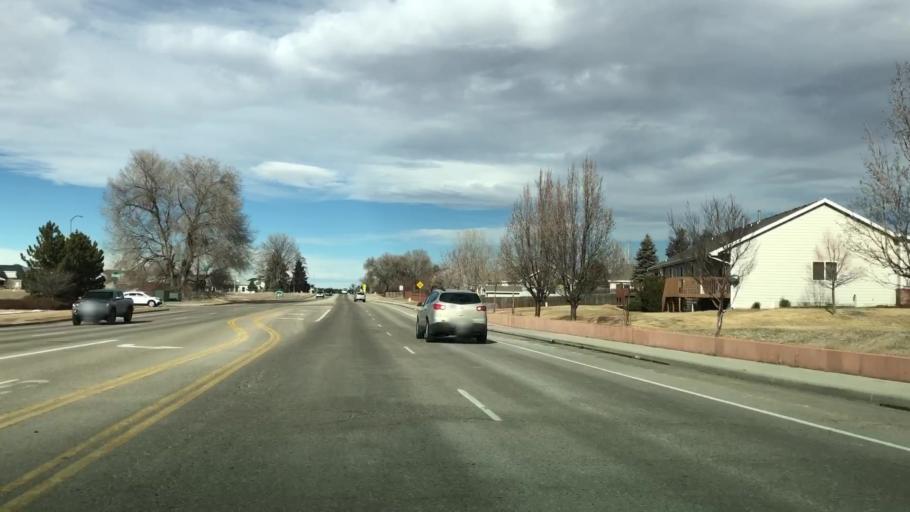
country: US
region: Colorado
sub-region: Weld County
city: Windsor
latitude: 40.4812
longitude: -104.9264
